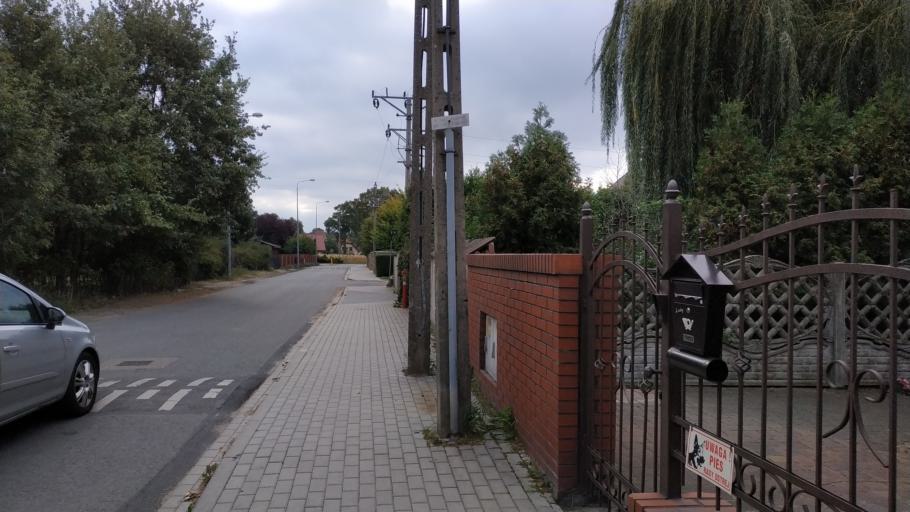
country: PL
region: Lower Silesian Voivodeship
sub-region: Powiat wroclawski
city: Tyniec Maly
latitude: 51.0201
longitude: 16.9155
